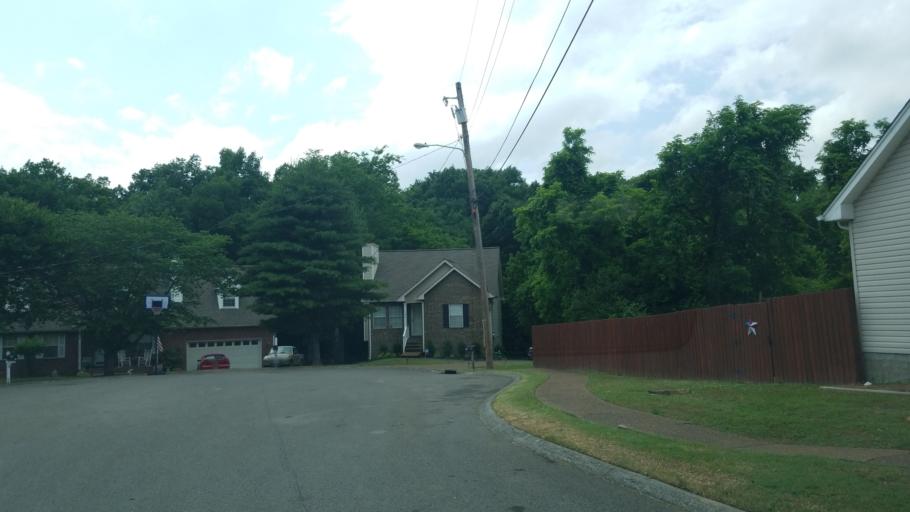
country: US
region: Tennessee
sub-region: Rutherford County
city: La Vergne
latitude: 36.0685
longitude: -86.6011
